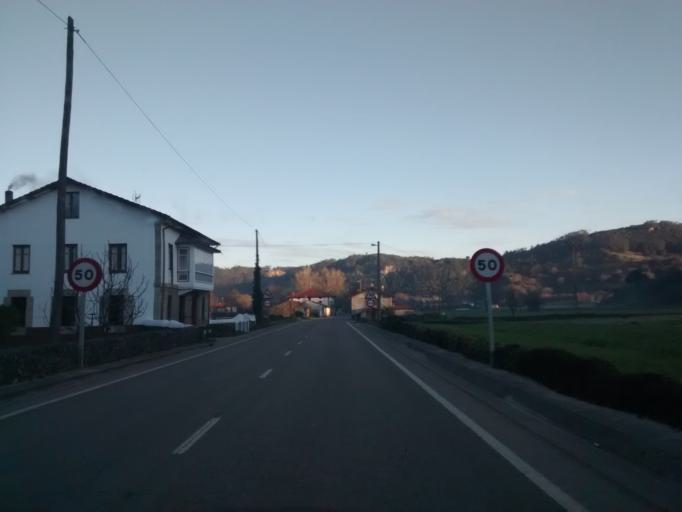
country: ES
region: Cantabria
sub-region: Provincia de Cantabria
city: Entrambasaguas
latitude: 43.3648
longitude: -3.7130
